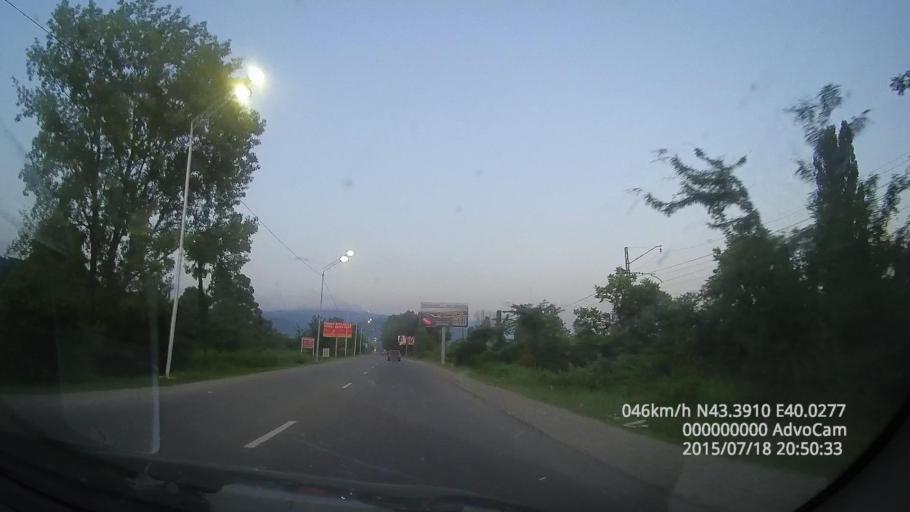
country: GE
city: Gantiadi
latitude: 43.3908
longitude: 40.0289
